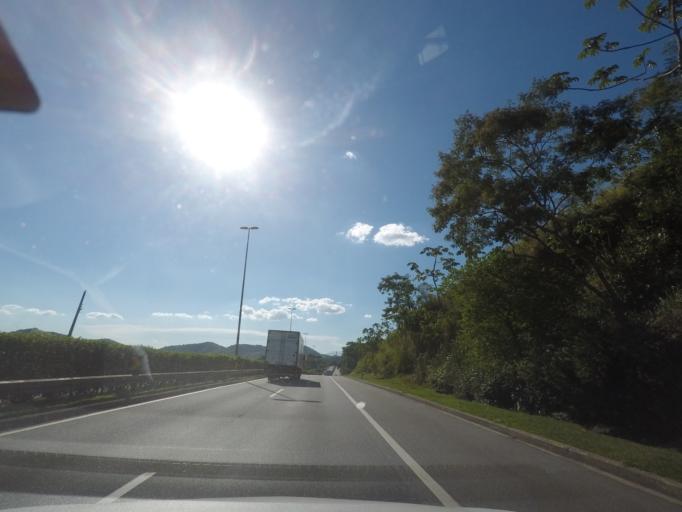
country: BR
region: Rio de Janeiro
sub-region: Sao Goncalo
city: Sao Goncalo
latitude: -22.6655
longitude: -43.1057
